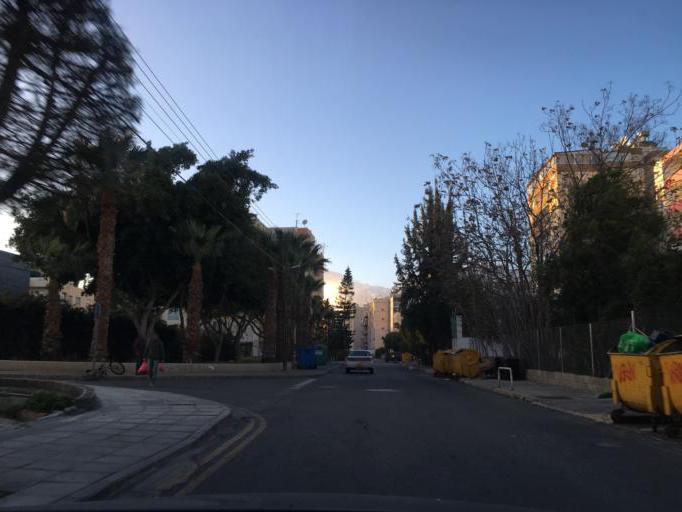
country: CY
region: Limassol
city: Limassol
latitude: 34.6913
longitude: 33.0678
